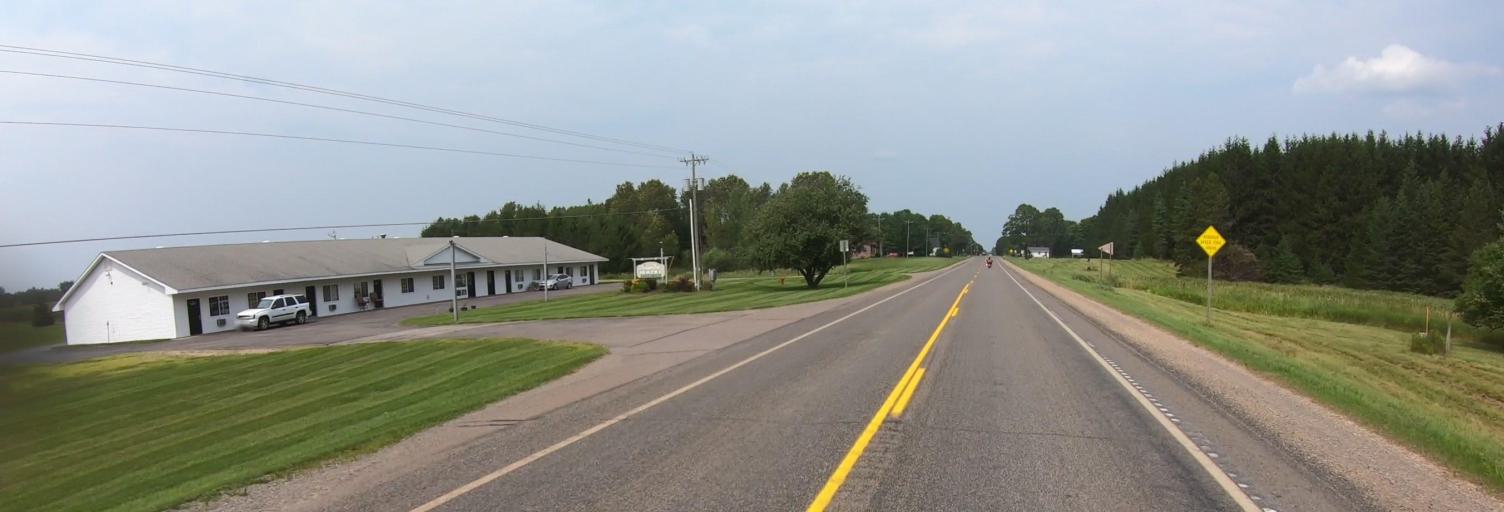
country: US
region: Michigan
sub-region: Alger County
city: Munising
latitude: 46.3410
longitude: -86.9289
